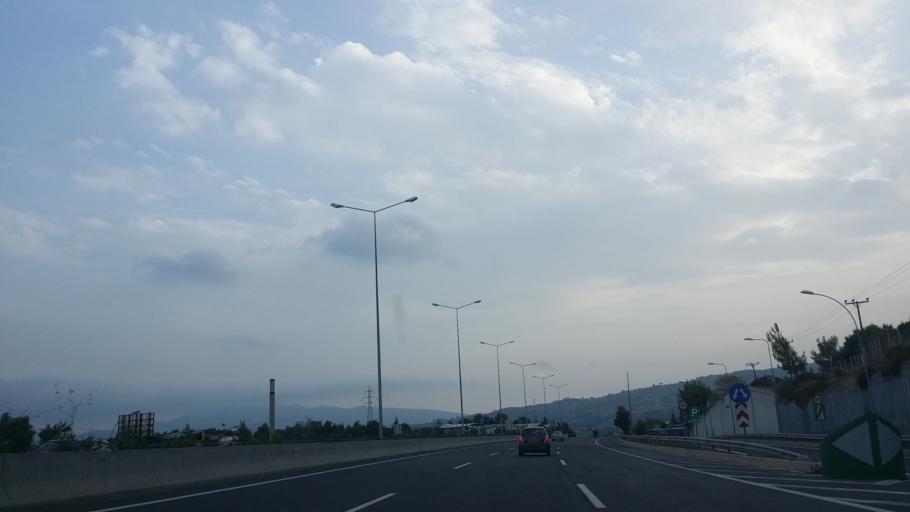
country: GR
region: Attica
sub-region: Nomarchia Anatolikis Attikis
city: Afidnes
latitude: 38.2048
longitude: 23.8548
